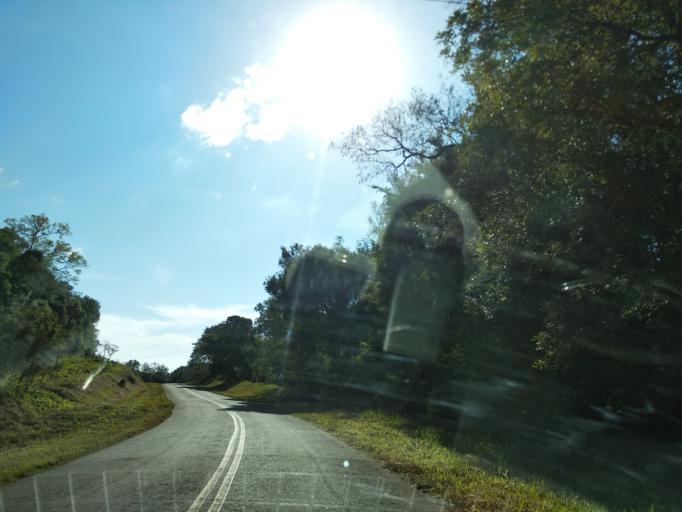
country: PY
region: Itapua
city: Hohenau
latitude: -27.0922
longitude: -55.6992
